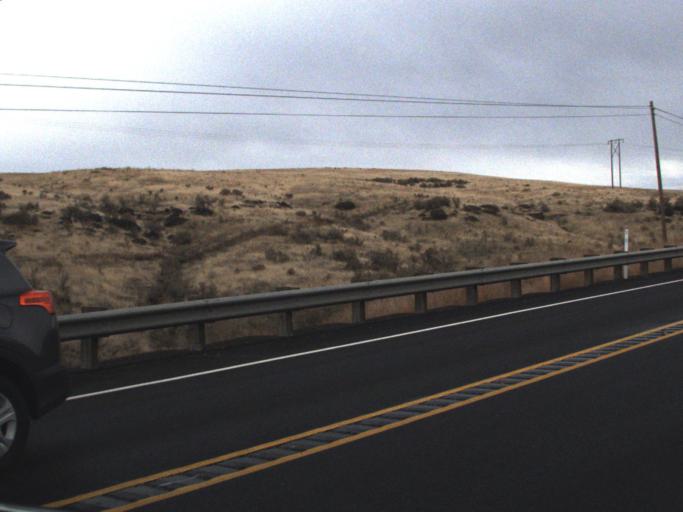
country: US
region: Washington
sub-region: Walla Walla County
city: Burbank
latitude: 46.0706
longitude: -118.7716
